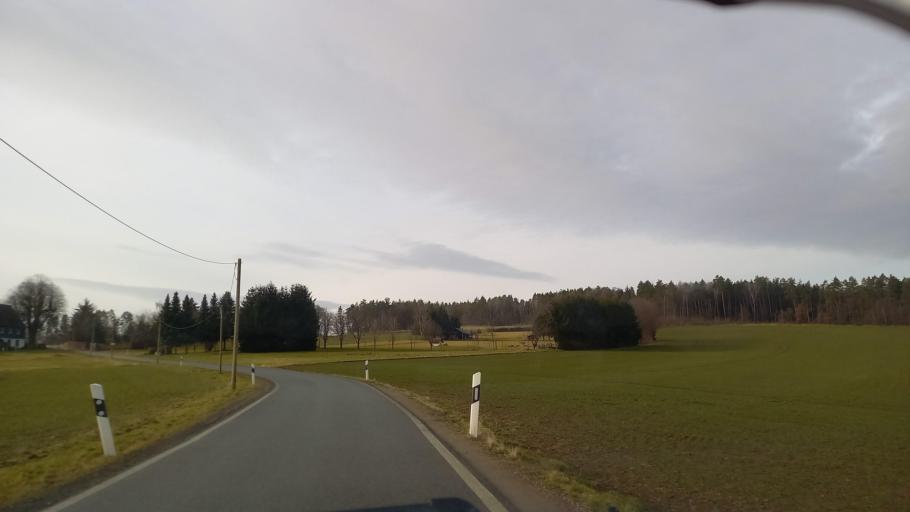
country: DE
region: Saxony
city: Kirchberg
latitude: 50.6129
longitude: 12.5140
